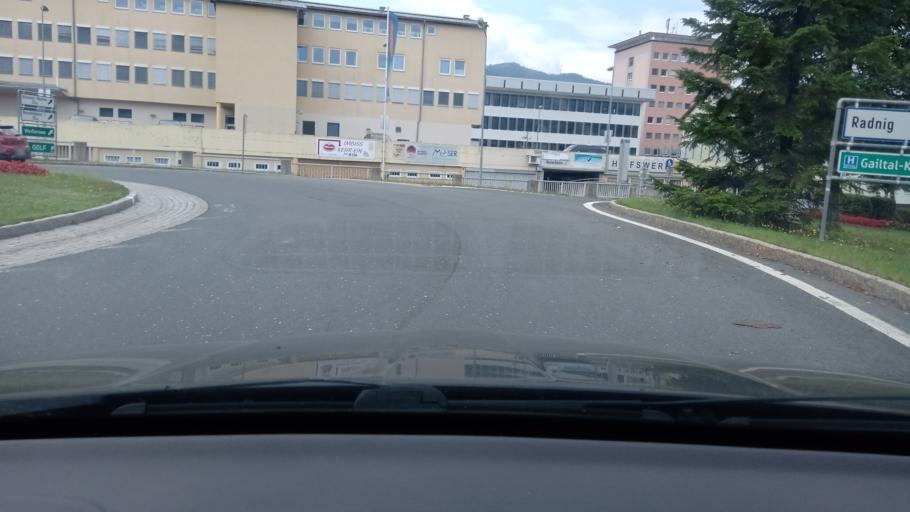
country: AT
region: Carinthia
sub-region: Politischer Bezirk Hermagor
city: Hermagor
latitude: 46.6258
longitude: 13.3734
